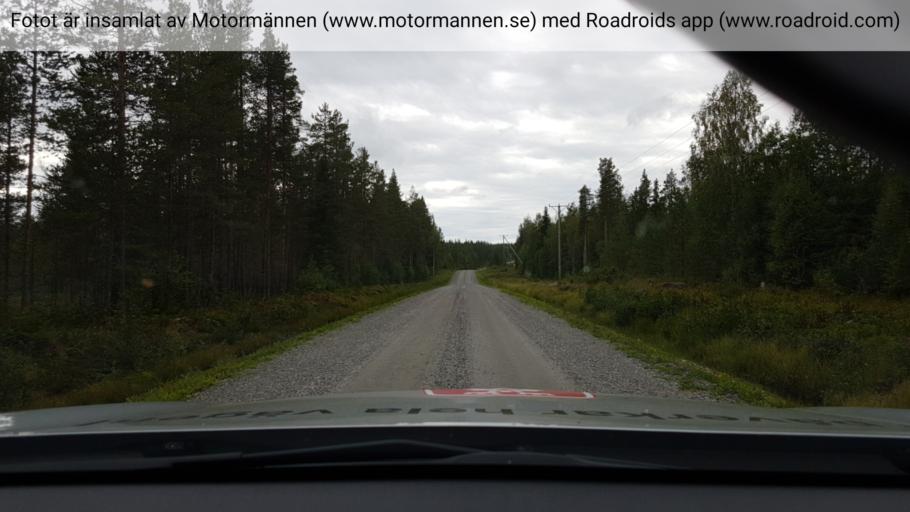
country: SE
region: Vaesterbotten
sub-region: Skelleftea Kommun
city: Langsele
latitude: 64.7311
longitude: 20.2784
